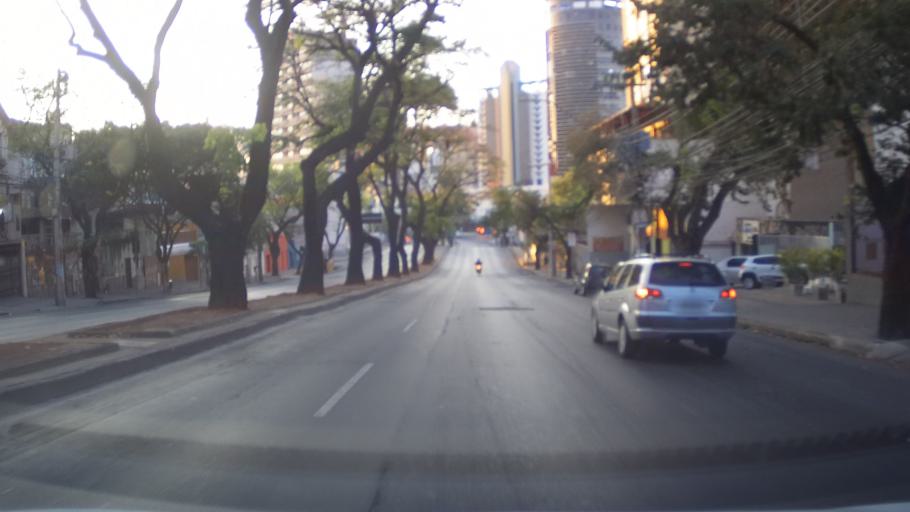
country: BR
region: Minas Gerais
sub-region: Belo Horizonte
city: Belo Horizonte
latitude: -19.9192
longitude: -43.9255
